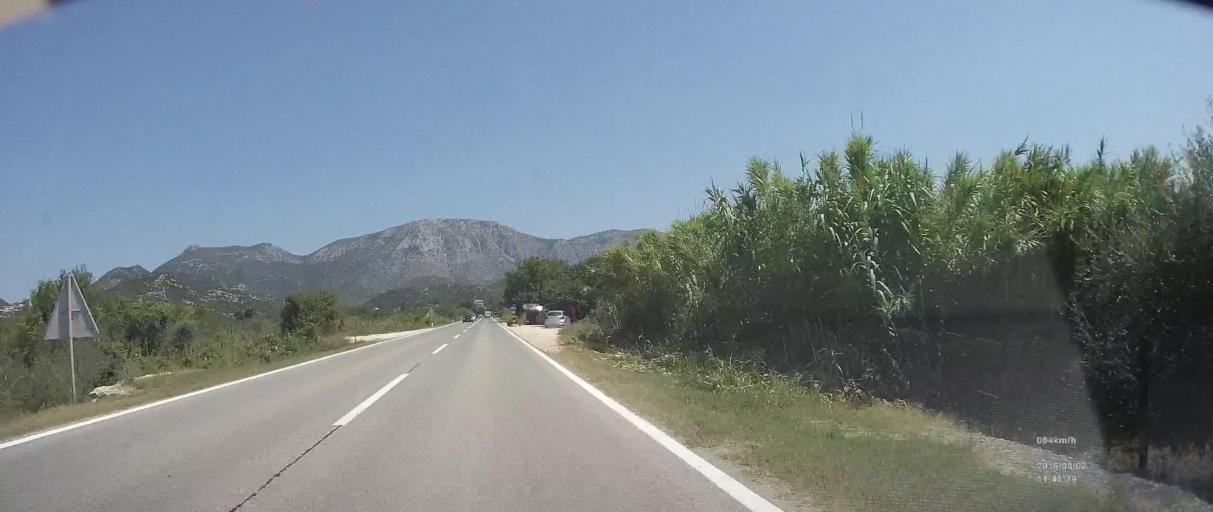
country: HR
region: Dubrovacko-Neretvanska
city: Komin
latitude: 43.0361
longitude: 17.4912
